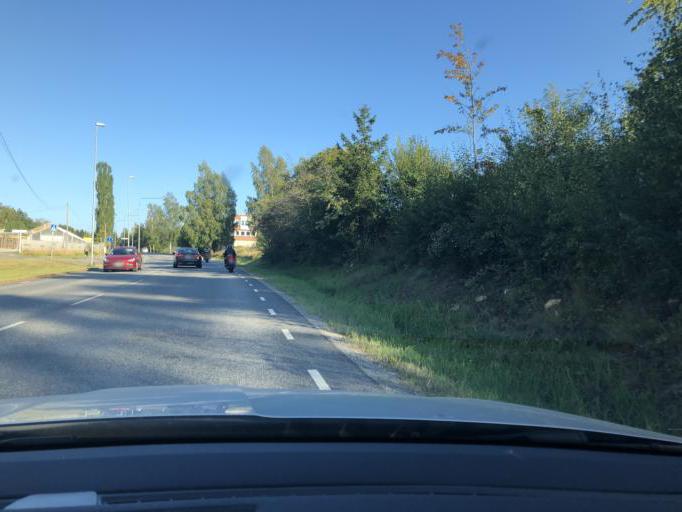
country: SE
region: Stockholm
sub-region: Sodertalje Kommun
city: Soedertaelje
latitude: 59.1838
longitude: 17.5936
